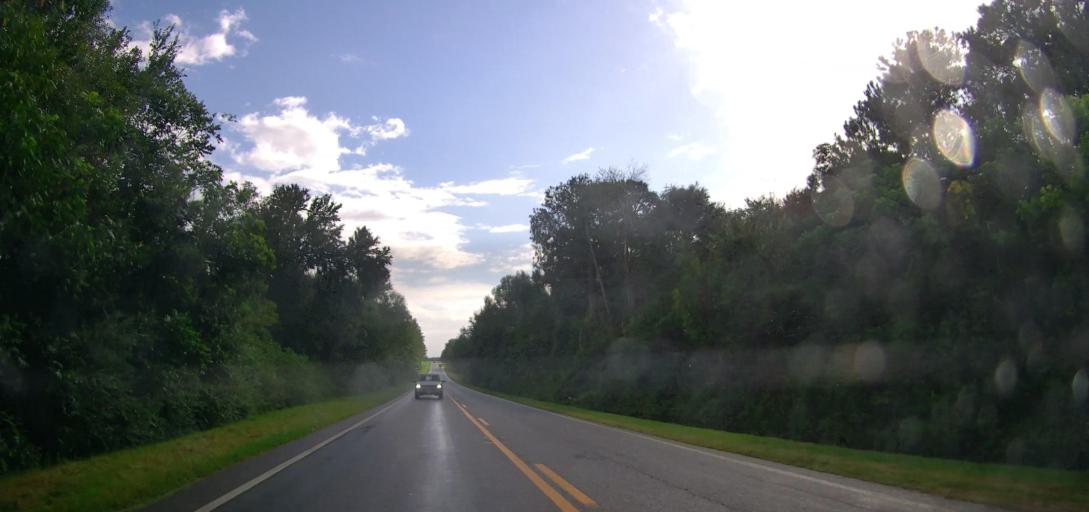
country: US
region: Georgia
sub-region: Coffee County
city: Douglas
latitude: 31.4803
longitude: -82.8677
